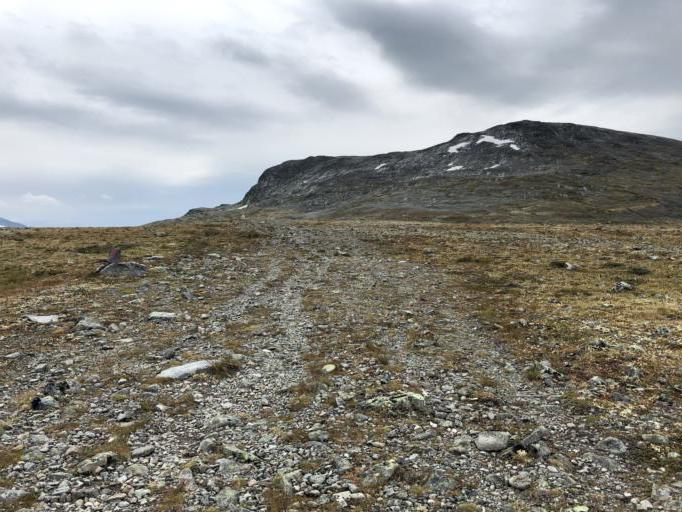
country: NO
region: Oppland
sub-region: Lom
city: Fossbergom
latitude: 61.5235
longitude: 8.8103
